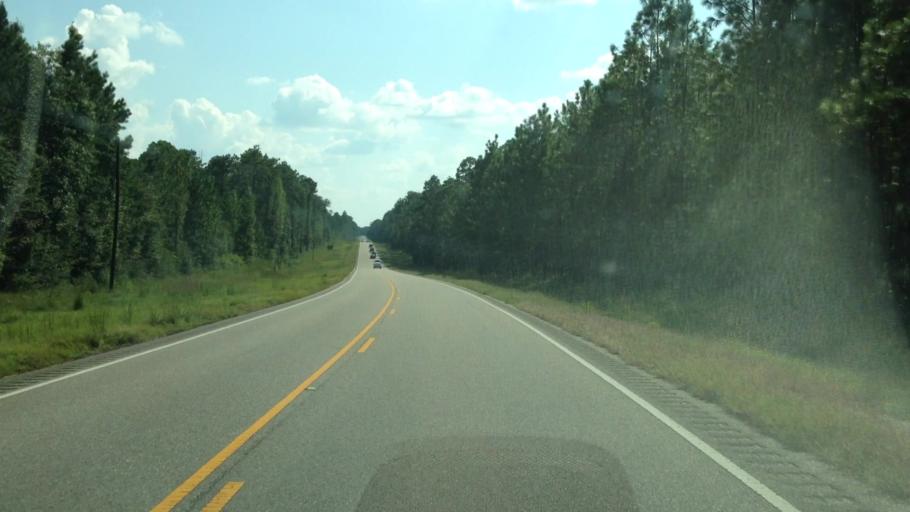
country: US
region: Florida
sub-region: Okaloosa County
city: Crestview
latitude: 31.0059
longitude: -86.6241
